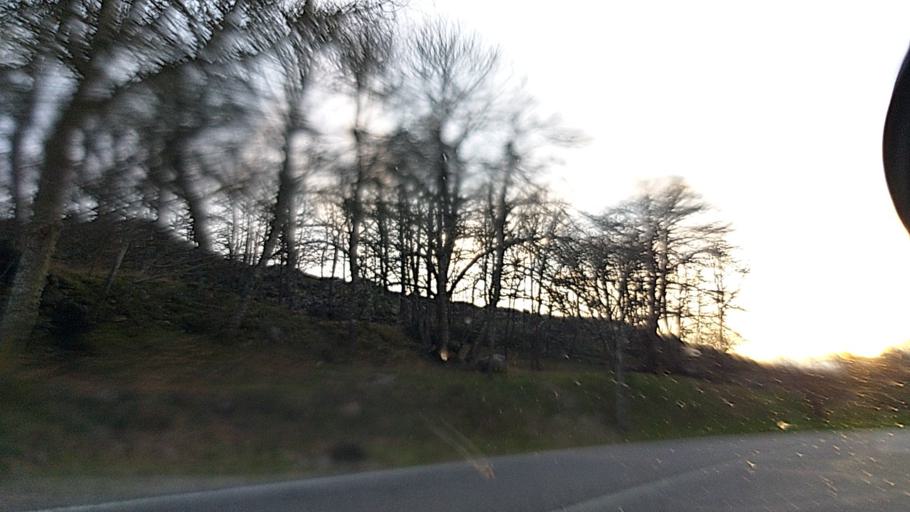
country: PT
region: Guarda
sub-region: Guarda
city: Sequeira
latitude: 40.5939
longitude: -7.1344
